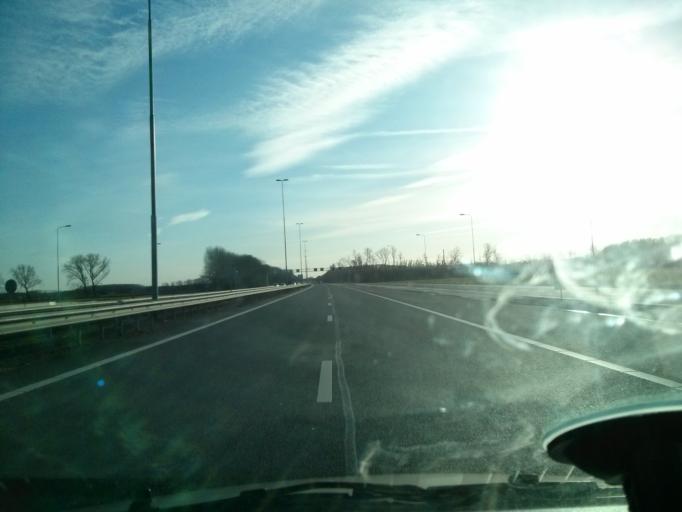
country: NL
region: Gelderland
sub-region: Gemeente Wijchen
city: Bergharen
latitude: 51.8550
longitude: 5.7072
